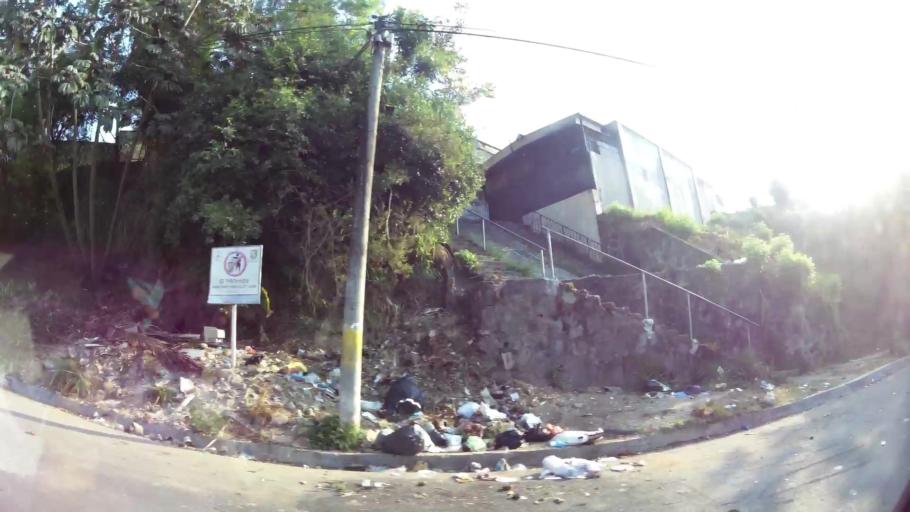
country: SV
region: San Salvador
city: San Salvador
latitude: 13.6782
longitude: -89.2035
